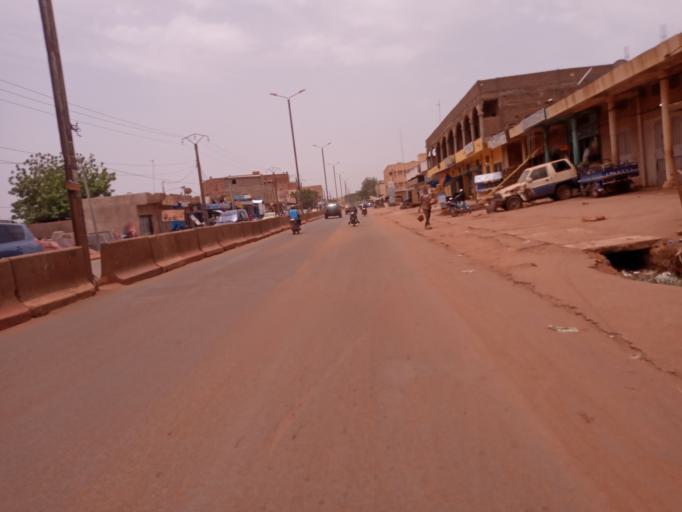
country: ML
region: Bamako
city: Bamako
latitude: 12.5926
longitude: -8.0190
